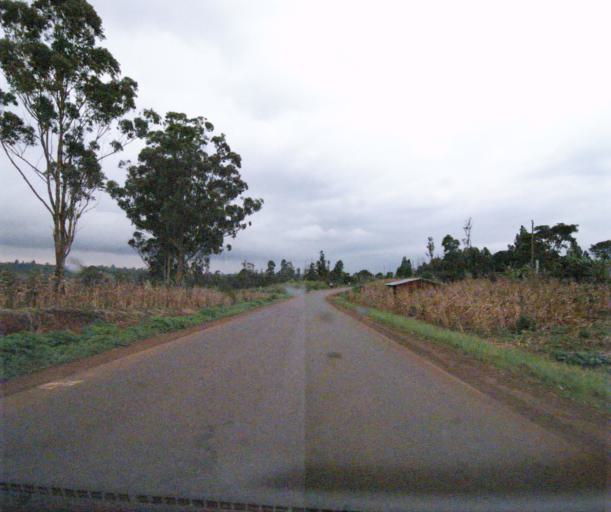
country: CM
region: West
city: Bansoa
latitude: 5.4900
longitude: 10.1967
